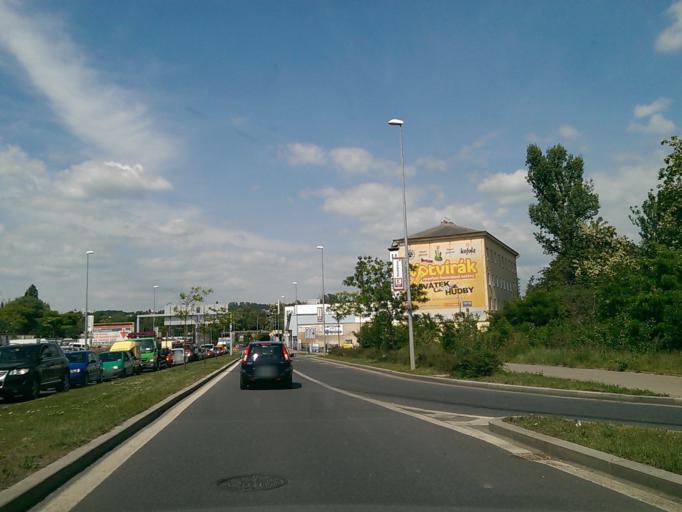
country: CZ
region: Praha
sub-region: Praha 8
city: Liben
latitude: 50.1003
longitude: 14.4664
